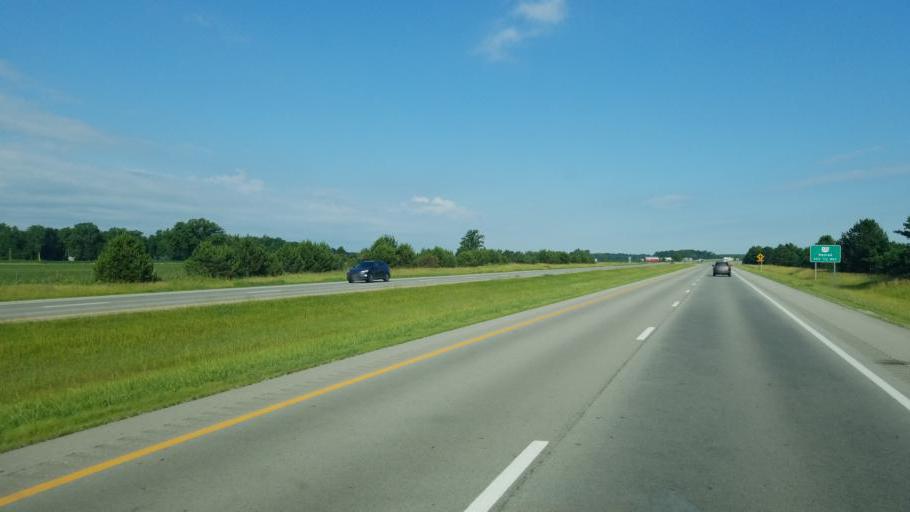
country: US
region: Ohio
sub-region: Wyandot County
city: Carey
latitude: 40.9643
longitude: -83.4727
